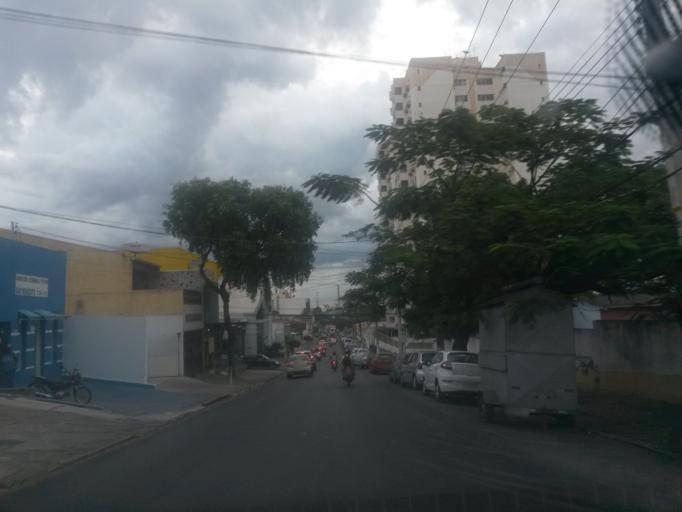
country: BR
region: Mato Grosso
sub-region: Cuiaba
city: Cuiaba
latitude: -15.6020
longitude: -56.0904
